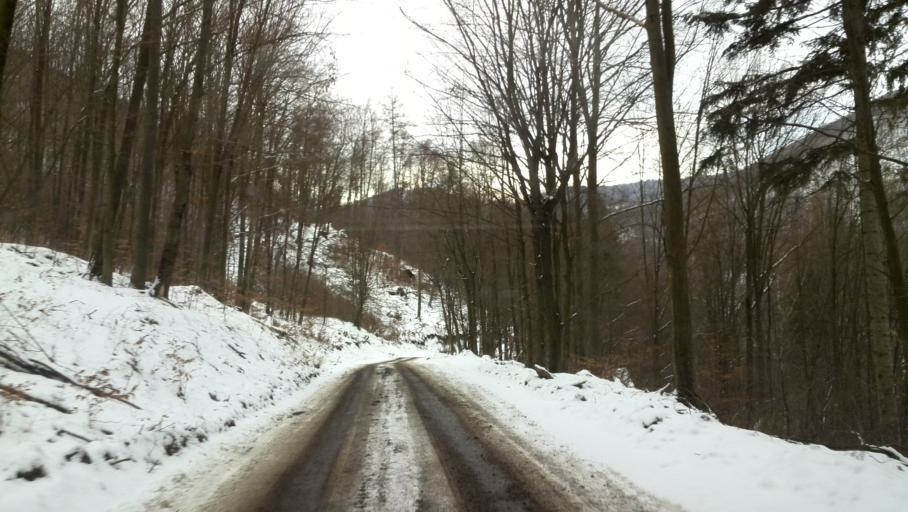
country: SK
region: Kosicky
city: Gelnica
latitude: 48.8157
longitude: 21.0661
